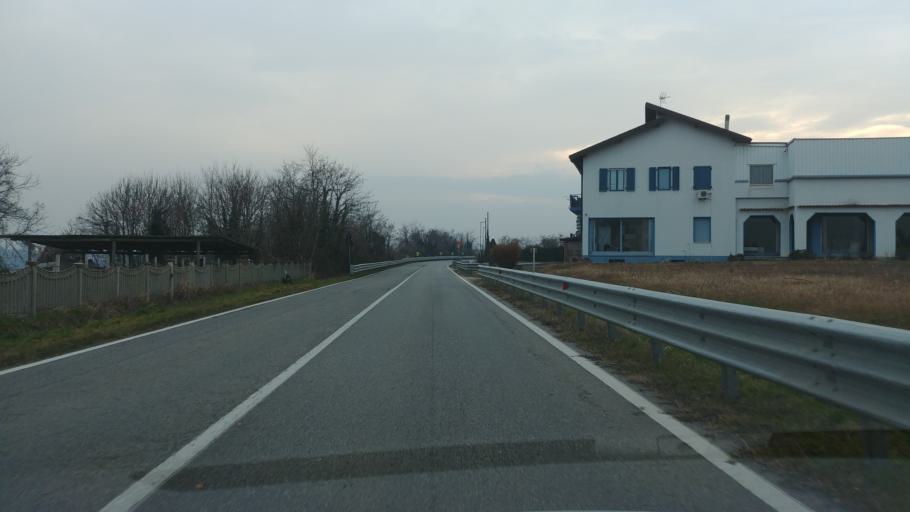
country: IT
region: Piedmont
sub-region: Provincia di Cuneo
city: Castelletto Stura
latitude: 44.4506
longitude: 7.6198
